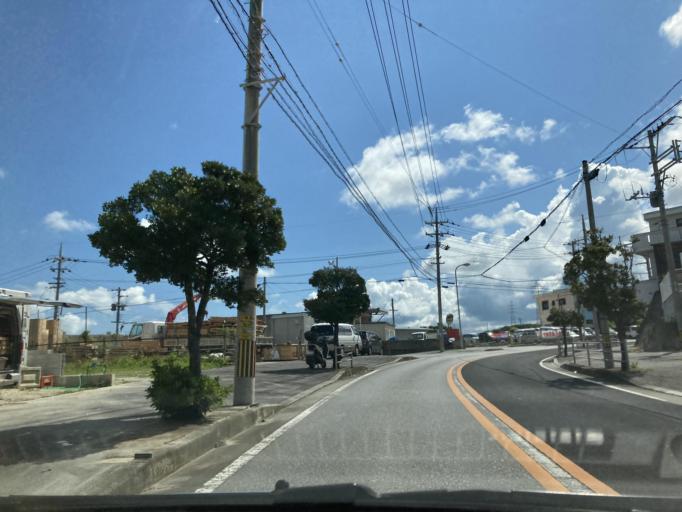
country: JP
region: Okinawa
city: Tomigusuku
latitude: 26.1657
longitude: 127.7218
